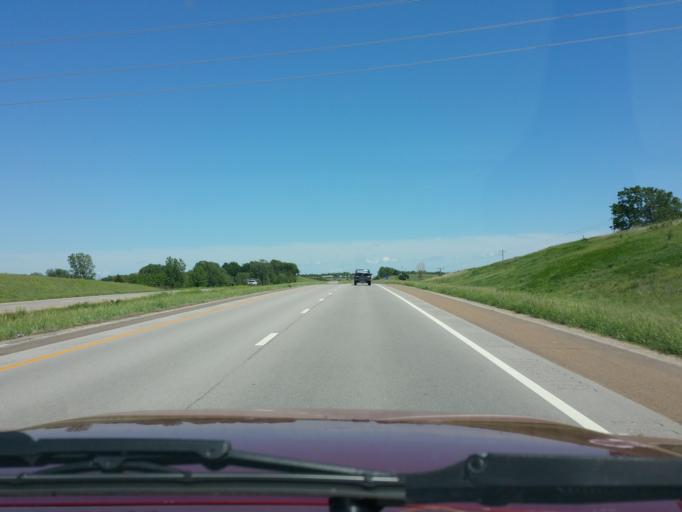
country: US
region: Kansas
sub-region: Pottawatomie County
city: Wamego
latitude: 39.2101
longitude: -96.3813
